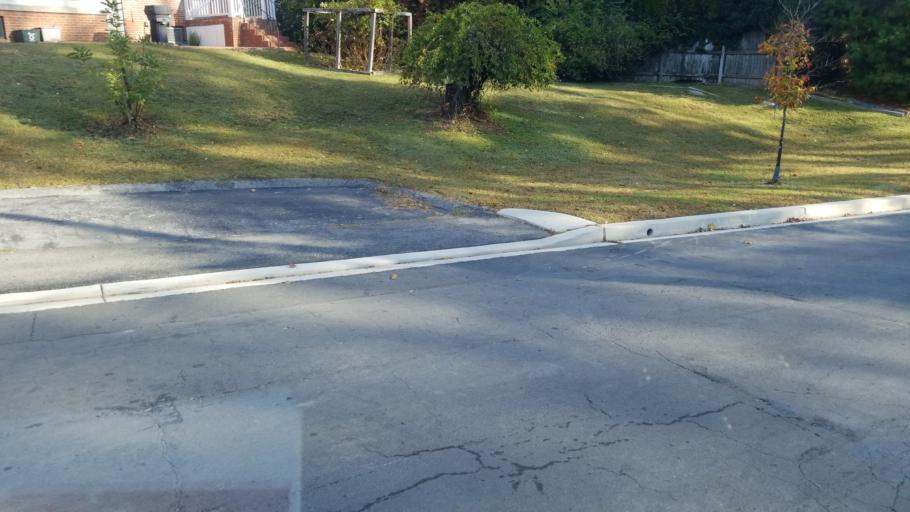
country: US
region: Maryland
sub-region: Montgomery County
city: Chevy Chase
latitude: 38.9698
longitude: -77.0549
